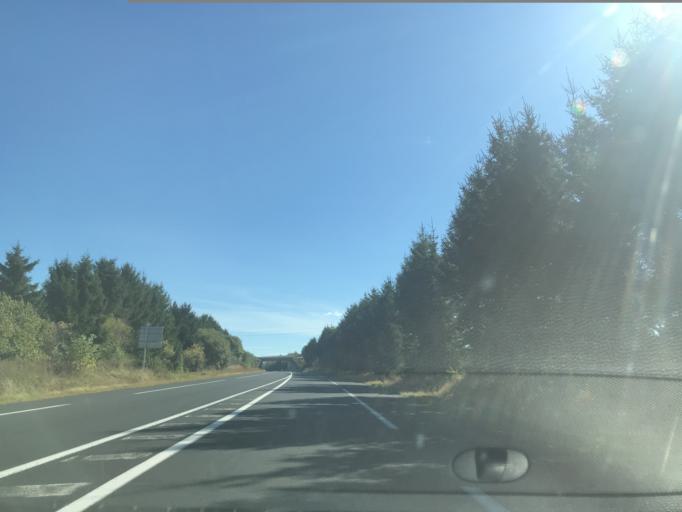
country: FR
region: Auvergne
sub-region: Departement du Puy-de-Dome
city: La Bourboule
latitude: 45.6619
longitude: 2.7528
